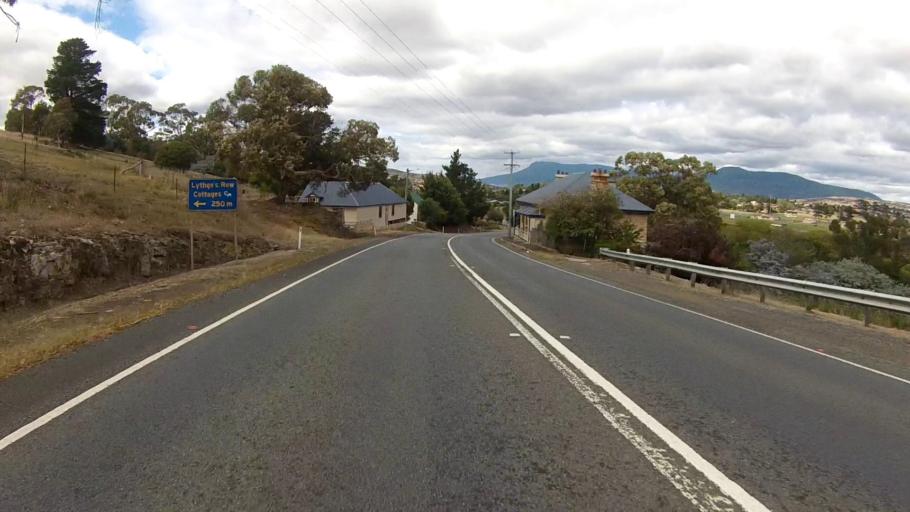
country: AU
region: Tasmania
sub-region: Brighton
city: Bridgewater
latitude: -42.6820
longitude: 147.2660
